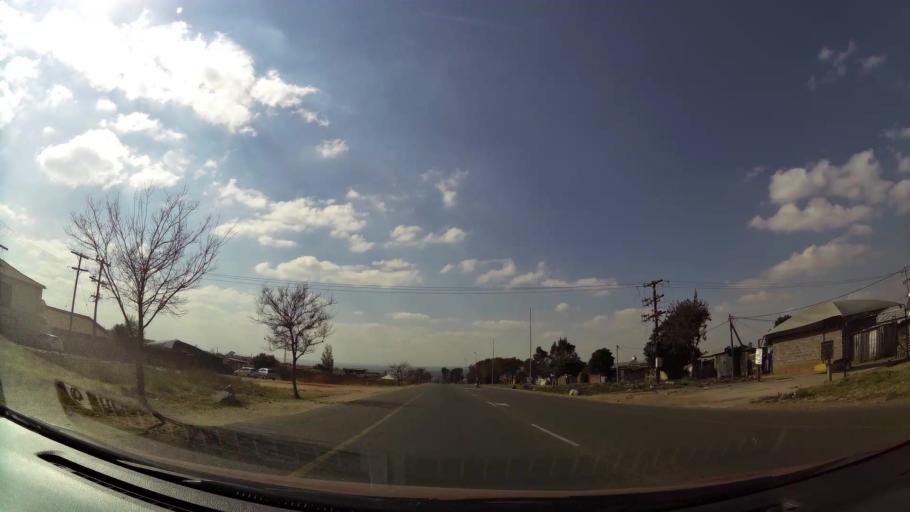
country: ZA
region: Gauteng
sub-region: City of Johannesburg Metropolitan Municipality
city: Midrand
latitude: -26.0072
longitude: 28.1736
